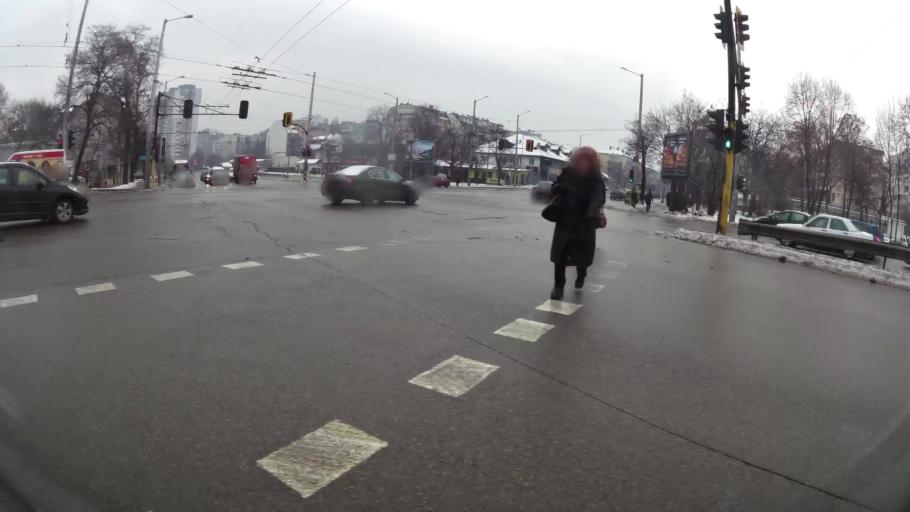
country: BG
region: Sofia-Capital
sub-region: Stolichna Obshtina
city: Sofia
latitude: 42.7075
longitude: 23.2990
